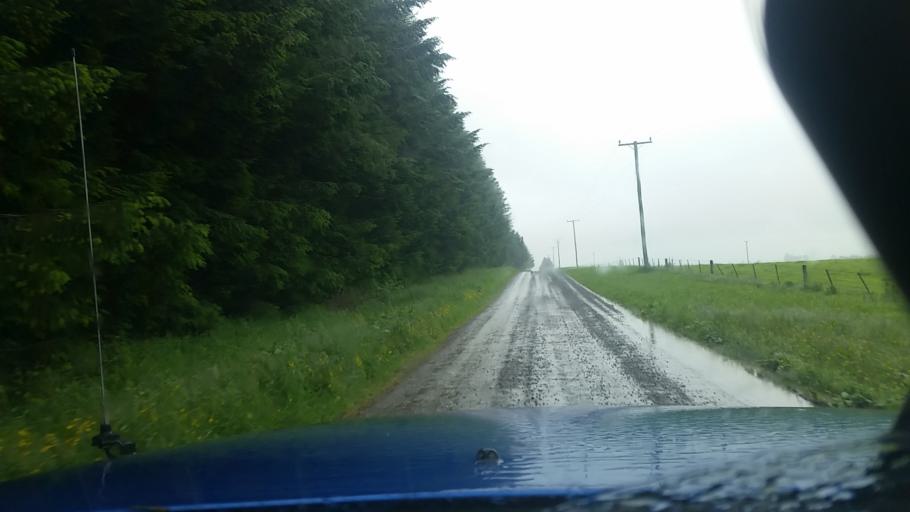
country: NZ
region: Canterbury
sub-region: Ashburton District
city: Methven
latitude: -43.5639
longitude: 171.5355
